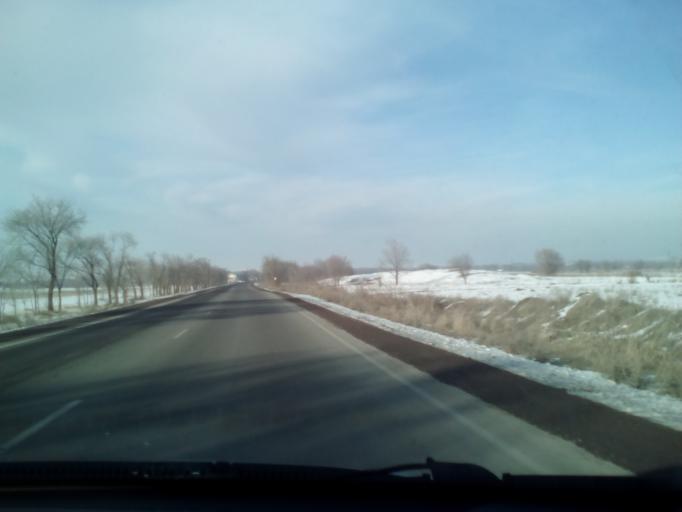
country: KZ
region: Almaty Oblysy
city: Burunday
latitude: 43.2082
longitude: 76.4150
